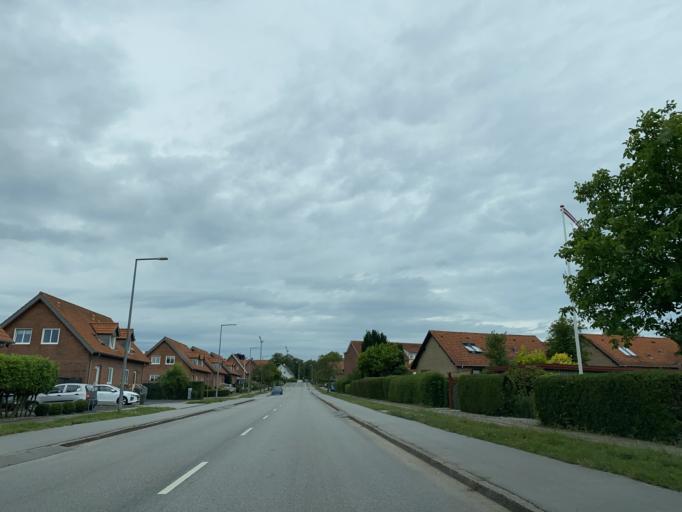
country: DK
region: South Denmark
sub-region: Sonderborg Kommune
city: Sonderborg
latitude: 54.9047
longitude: 9.8050
